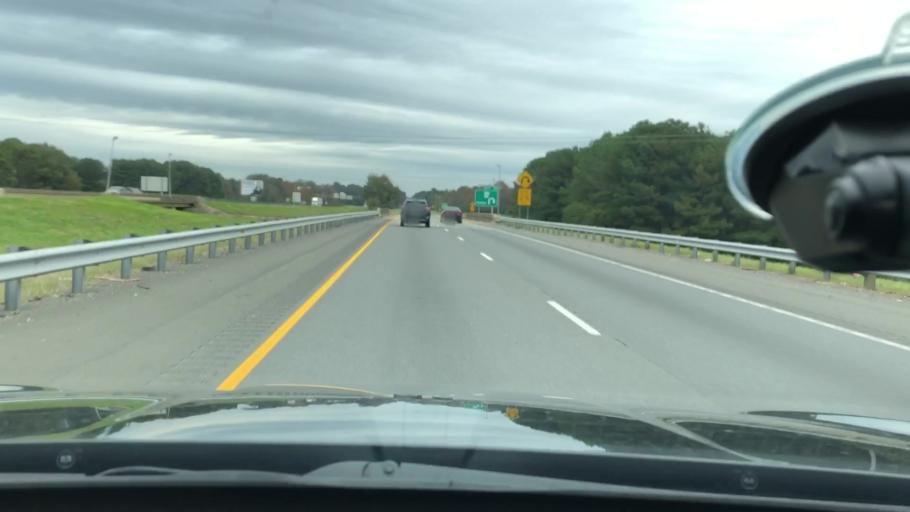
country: US
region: Arkansas
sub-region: Hempstead County
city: Hope
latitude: 33.6901
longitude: -93.5991
